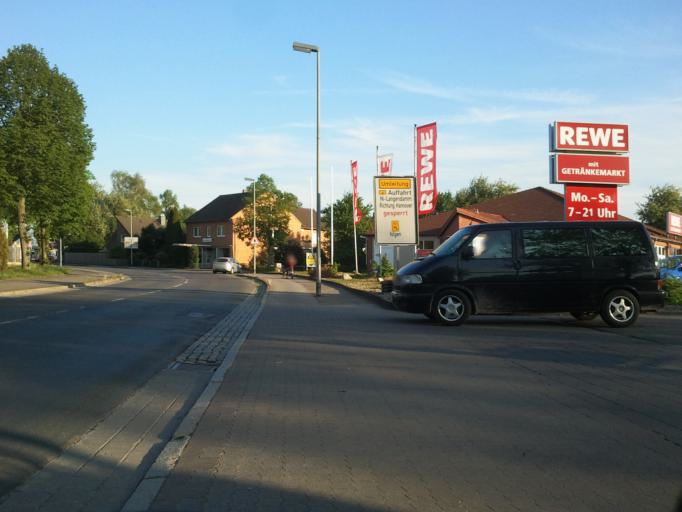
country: DE
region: Lower Saxony
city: Nienburg
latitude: 52.6313
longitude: 9.2160
